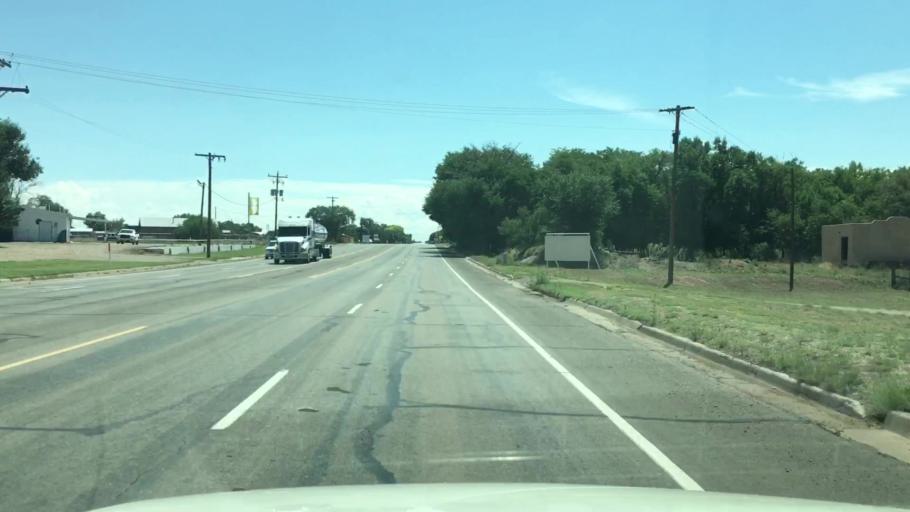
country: US
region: New Mexico
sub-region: De Baca County
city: Fort Sumner
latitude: 34.4681
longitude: -104.2344
